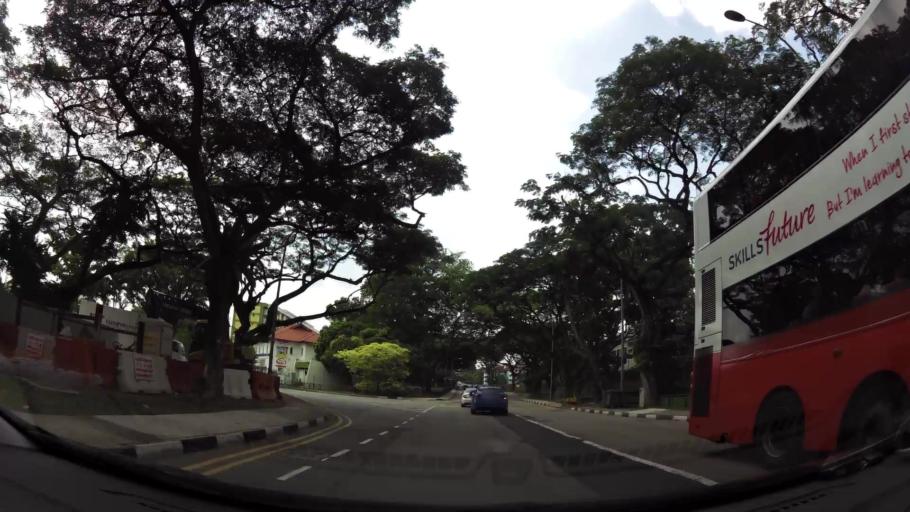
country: SG
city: Singapore
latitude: 1.2762
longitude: 103.8318
